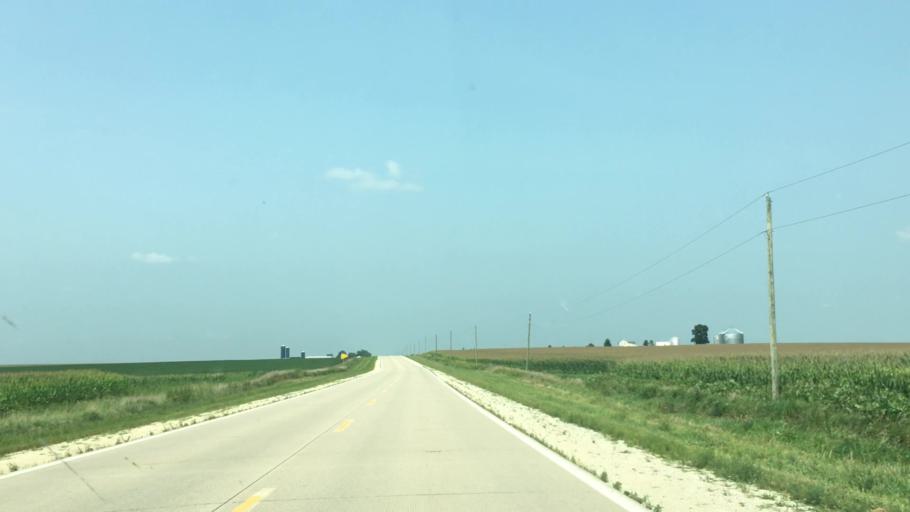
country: US
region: Iowa
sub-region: Fayette County
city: Fayette
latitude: 42.7295
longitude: -91.8041
